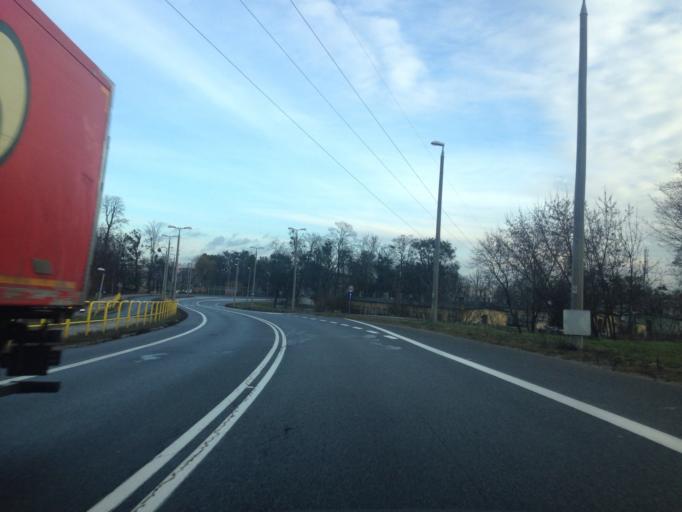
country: PL
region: Kujawsko-Pomorskie
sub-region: Torun
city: Torun
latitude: 52.9889
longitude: 18.5998
